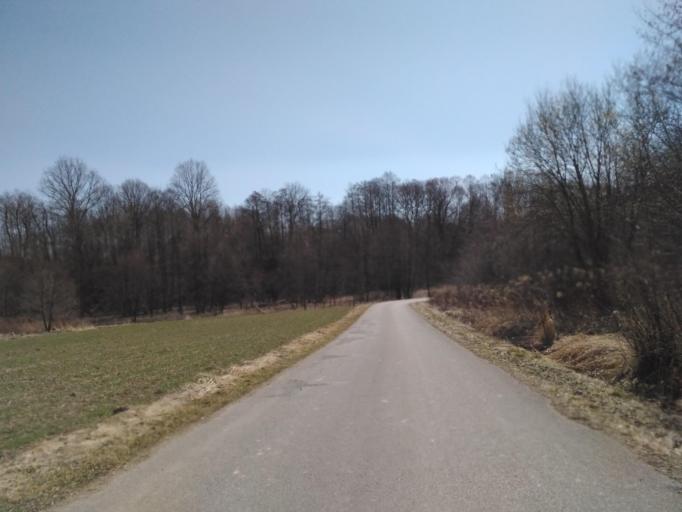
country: PL
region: Subcarpathian Voivodeship
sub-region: Powiat brzozowski
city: Orzechowka
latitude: 49.7118
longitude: 21.9683
